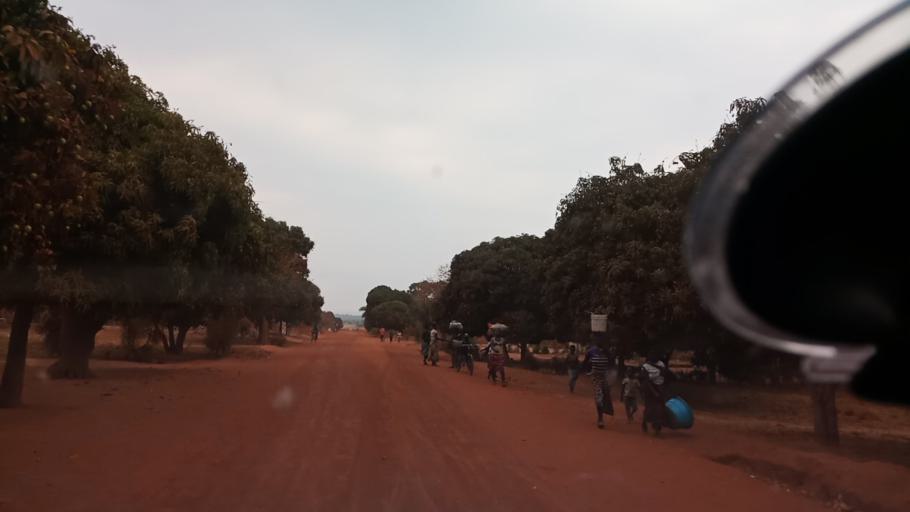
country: ZM
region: Luapula
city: Nchelenge
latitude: -9.2771
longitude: 28.3241
